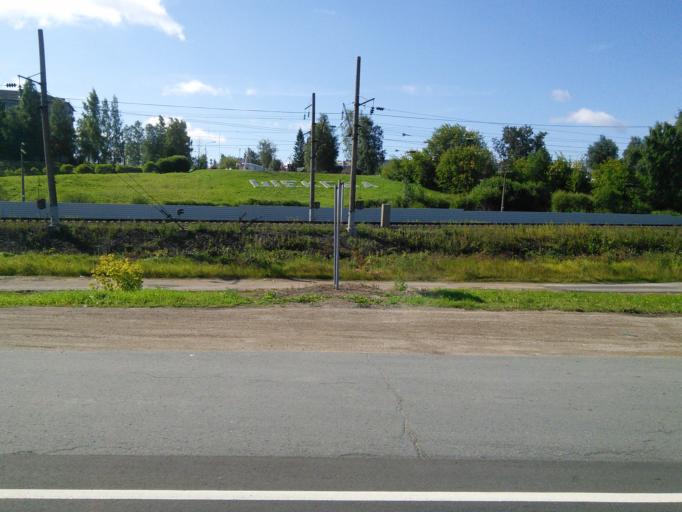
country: RU
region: Vologda
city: Sheksna
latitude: 59.2099
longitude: 38.5015
